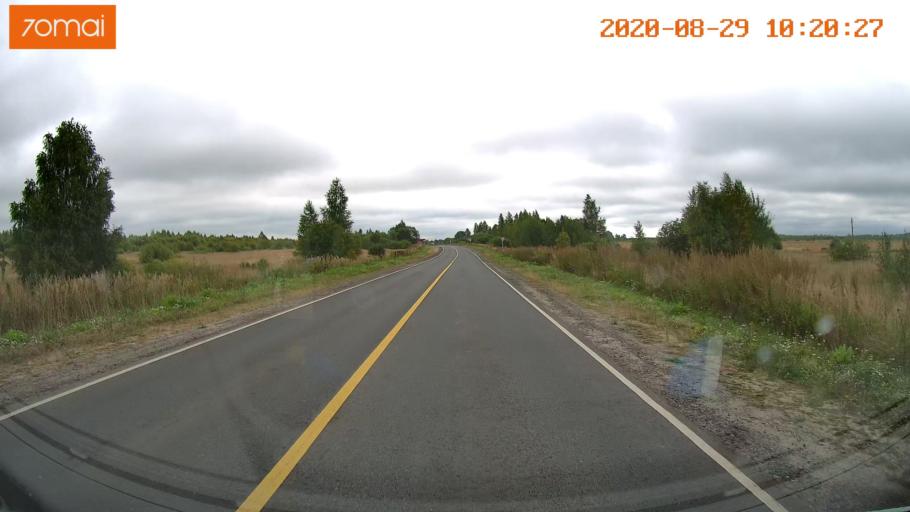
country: RU
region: Ivanovo
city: Yur'yevets
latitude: 57.3237
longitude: 42.8858
